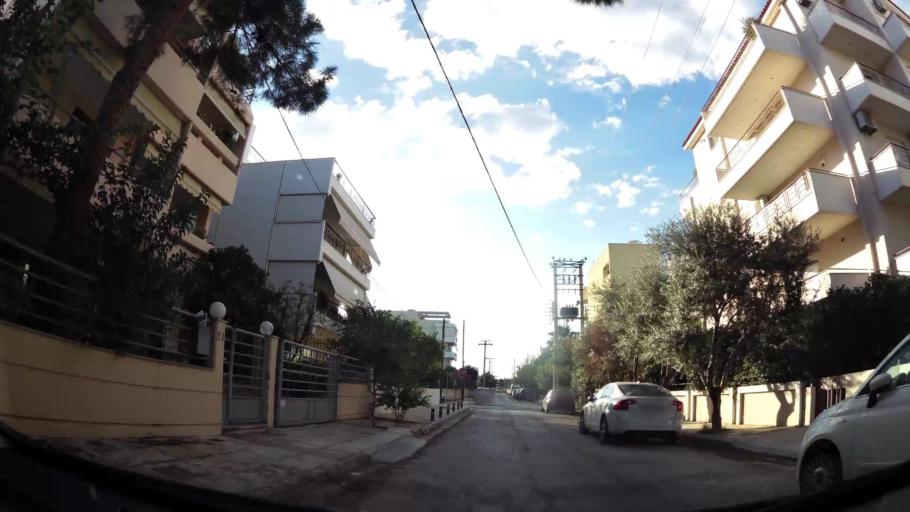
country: GR
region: Attica
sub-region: Nomarchia Athinas
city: Elliniko
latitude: 37.8894
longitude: 23.7453
